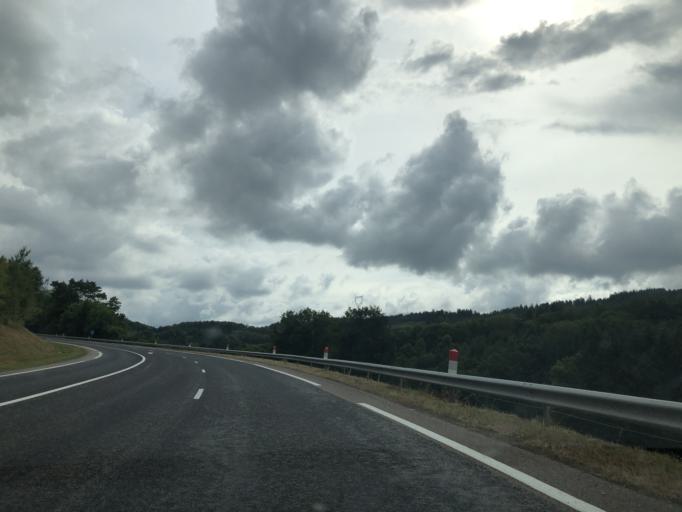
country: FR
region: Lorraine
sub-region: Departement des Vosges
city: Anould
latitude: 48.1777
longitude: 6.9297
